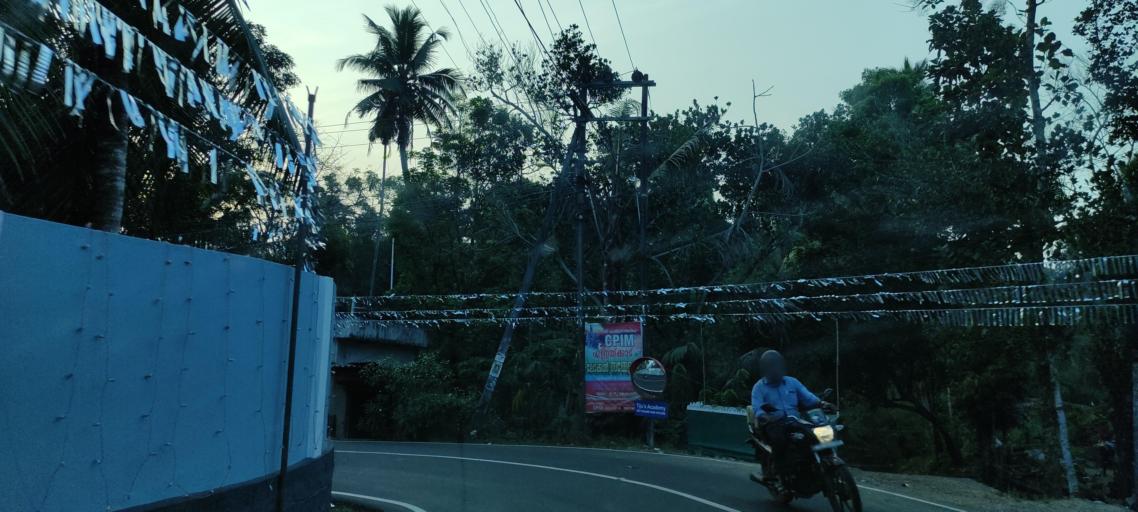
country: IN
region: Kerala
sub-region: Alappuzha
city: Mavelikara
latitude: 9.2682
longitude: 76.5468
